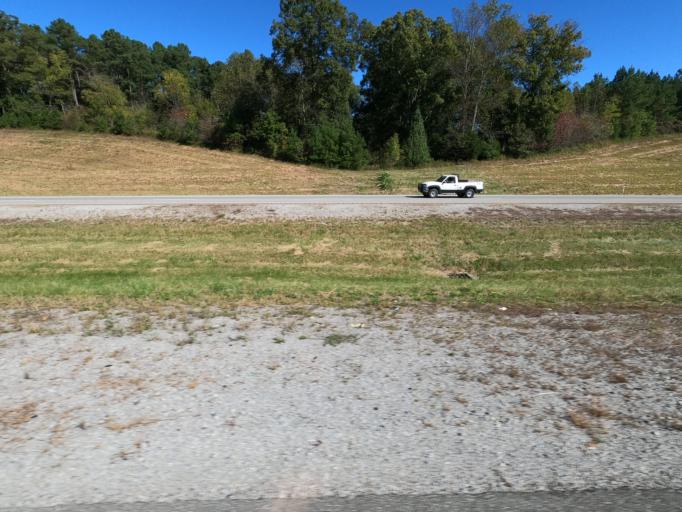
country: US
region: Tennessee
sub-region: Williamson County
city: Fairview
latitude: 35.8980
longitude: -87.1372
